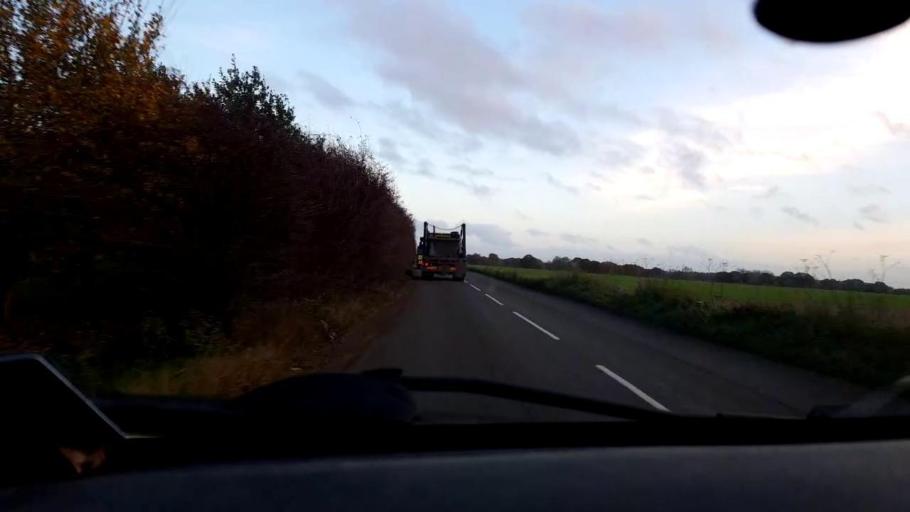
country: GB
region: England
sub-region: Norfolk
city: Mattishall
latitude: 52.6932
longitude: 1.0954
